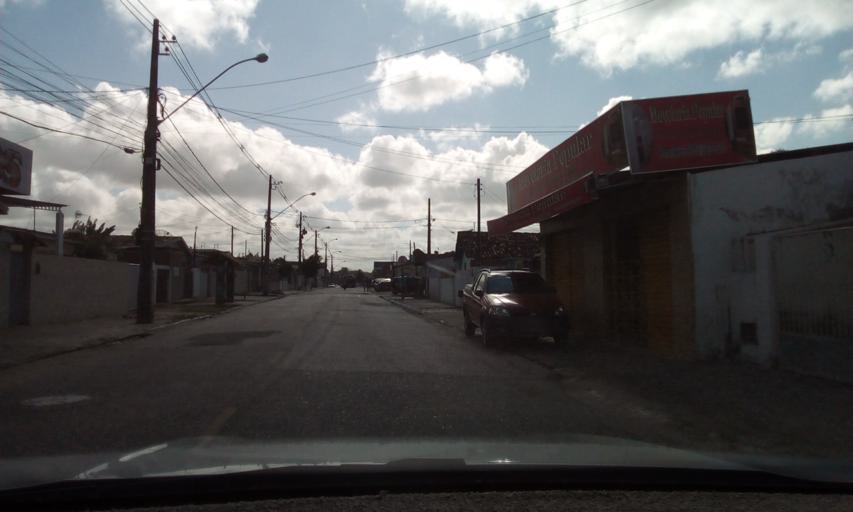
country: BR
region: Paraiba
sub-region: Bayeux
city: Bayeux
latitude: -7.1557
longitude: -34.9015
